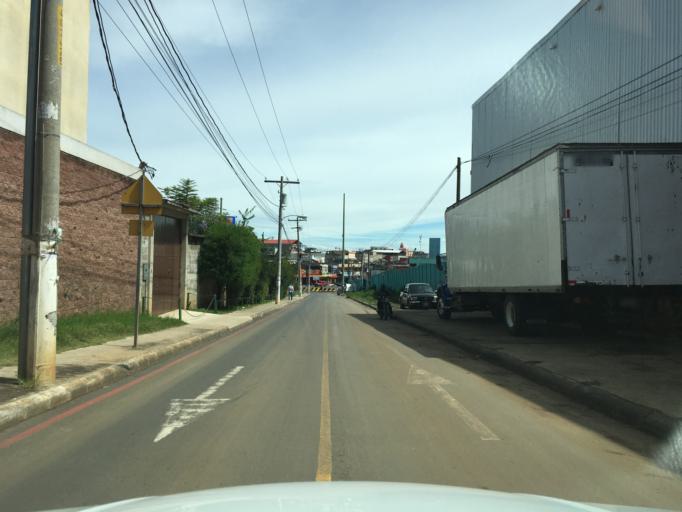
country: GT
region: Guatemala
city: Mixco
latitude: 14.6593
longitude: -90.5633
